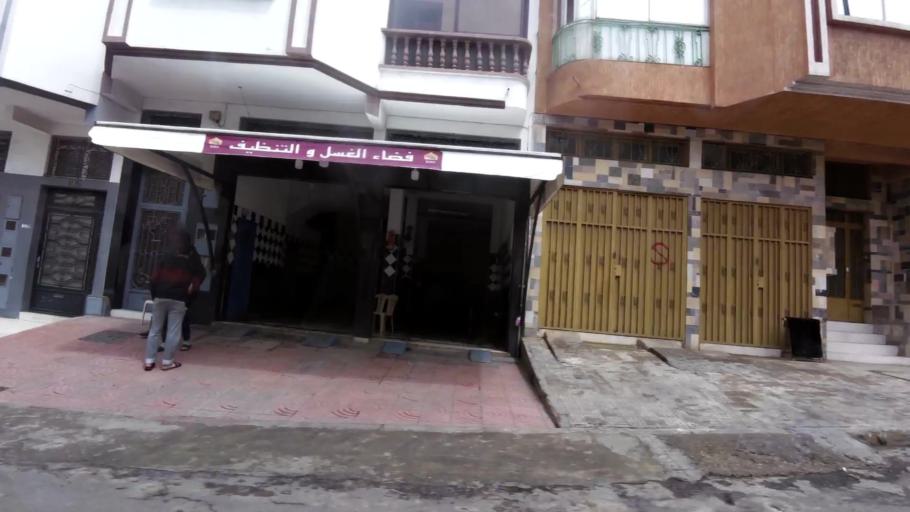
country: MA
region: Grand Casablanca
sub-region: Casablanca
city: Casablanca
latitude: 33.5406
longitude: -7.6766
